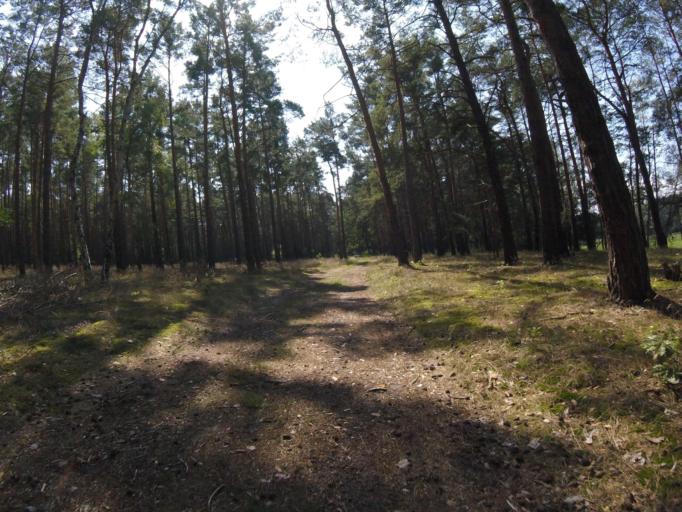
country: DE
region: Brandenburg
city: Bestensee
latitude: 52.2198
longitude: 13.6953
